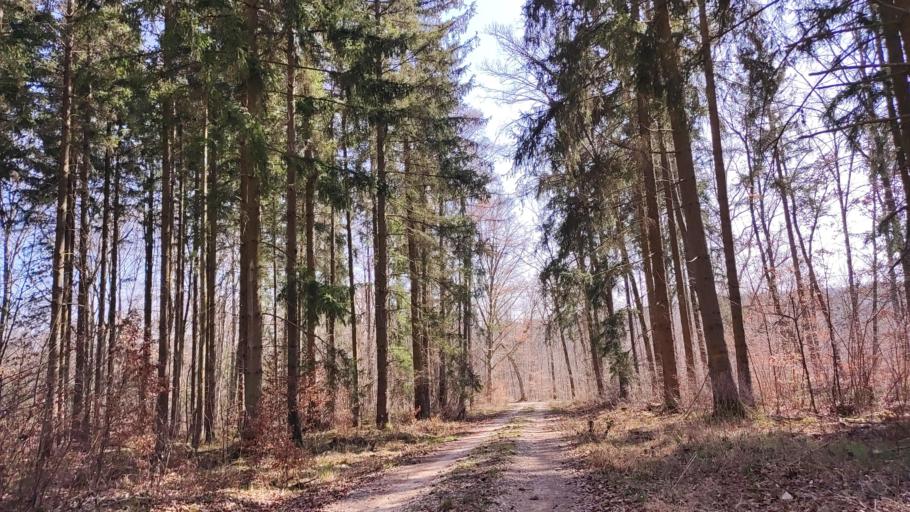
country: DE
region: Baden-Wuerttemberg
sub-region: Tuebingen Region
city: Borslingen
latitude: 48.5208
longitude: 10.0454
